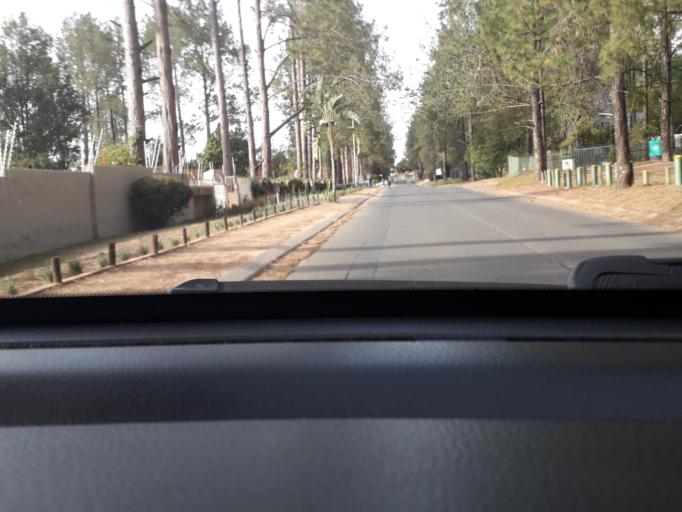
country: ZA
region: Gauteng
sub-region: City of Johannesburg Metropolitan Municipality
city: Diepsloot
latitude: -26.0404
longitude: 28.0302
